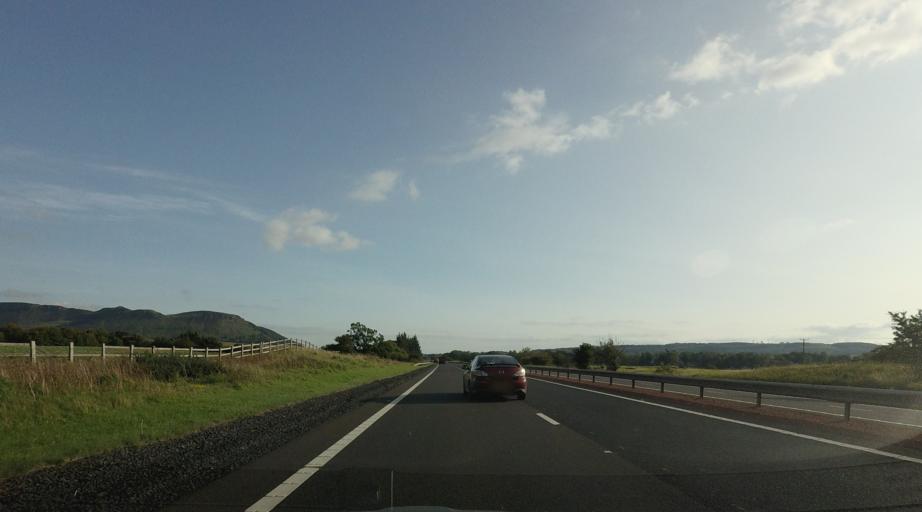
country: GB
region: Scotland
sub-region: Perth and Kinross
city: Kinross
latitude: 56.1834
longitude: -3.4160
